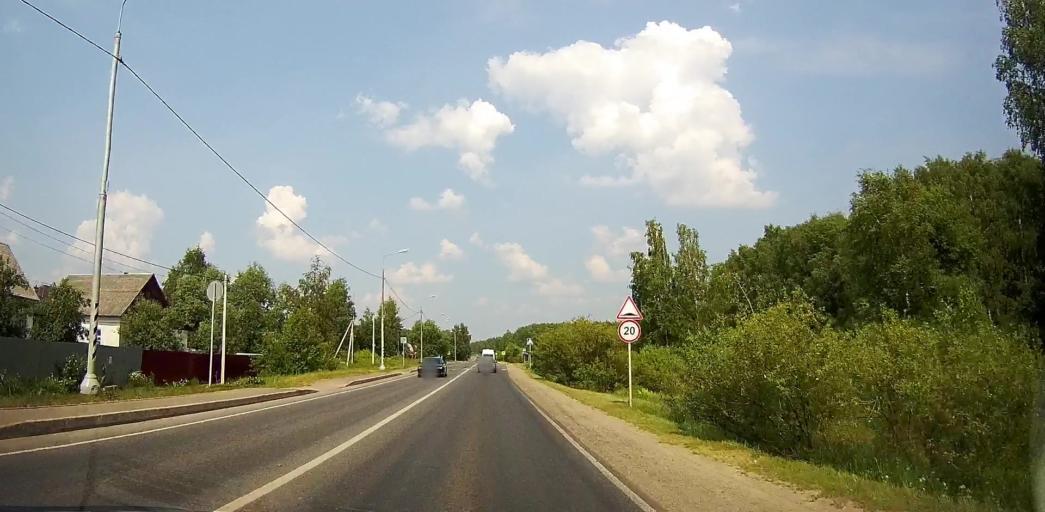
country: RU
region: Moskovskaya
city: Stupino
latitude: 54.9161
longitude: 38.1036
